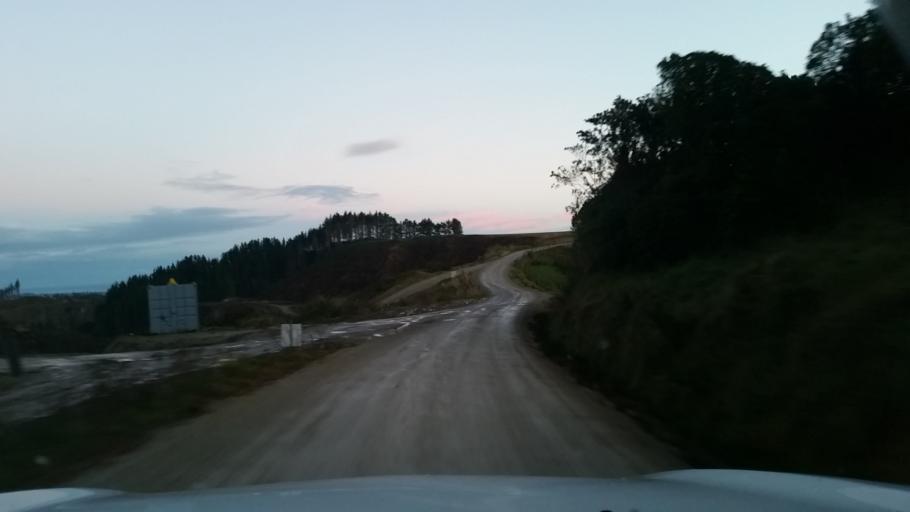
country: NZ
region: Manawatu-Wanganui
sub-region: Wanganui District
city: Wanganui
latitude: -39.7718
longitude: 174.8708
